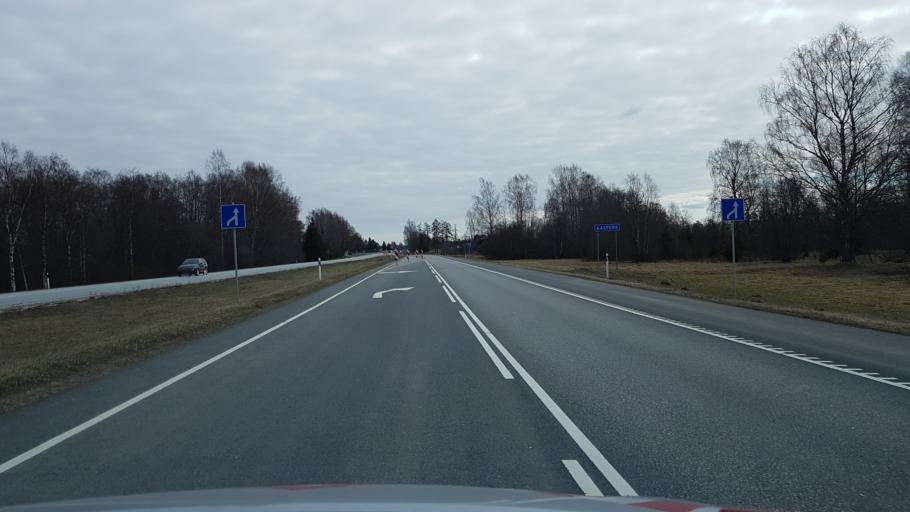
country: EE
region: Laeaene-Virumaa
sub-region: Kadrina vald
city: Kadrina
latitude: 59.4396
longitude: 26.1272
